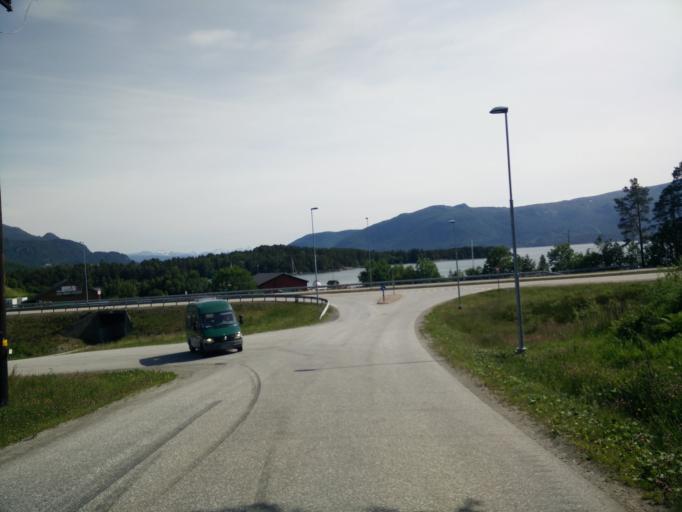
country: NO
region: More og Romsdal
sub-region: Kristiansund
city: Rensvik
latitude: 63.0117
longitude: 7.9701
